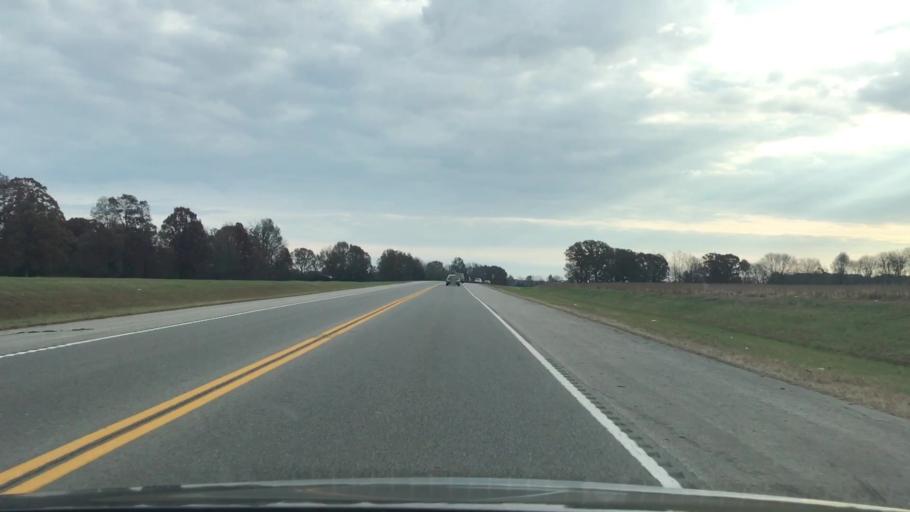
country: US
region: Tennessee
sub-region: Macon County
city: Lafayette
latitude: 36.4976
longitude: -85.9752
